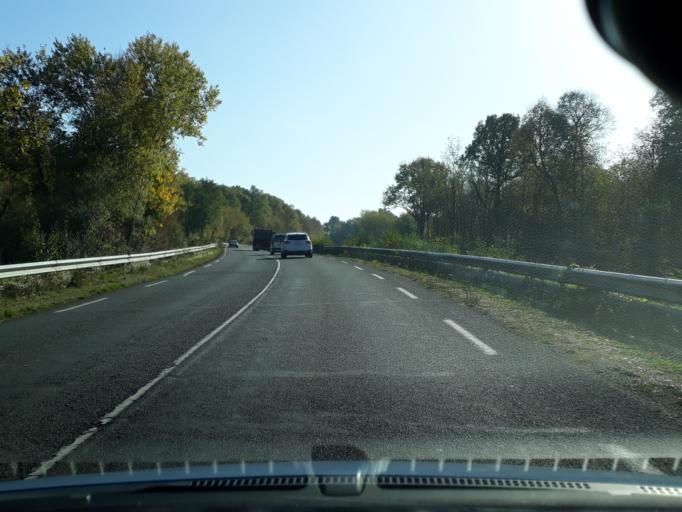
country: FR
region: Ile-de-France
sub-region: Departement de Seine-et-Marne
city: Livry-sur-Seine
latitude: 48.5018
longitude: 2.6848
